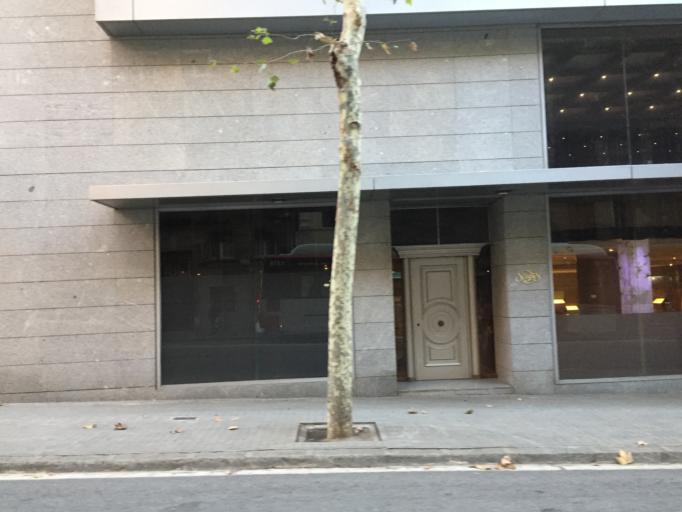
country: ES
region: Catalonia
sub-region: Provincia de Barcelona
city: Sants-Montjuic
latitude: 41.3725
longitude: 2.1553
